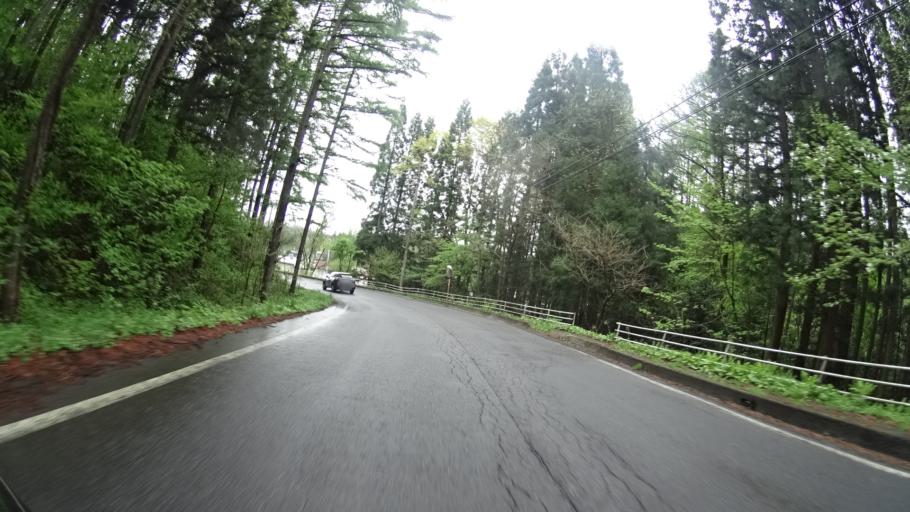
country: JP
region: Nagano
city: Nagano-shi
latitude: 36.7665
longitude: 138.1986
